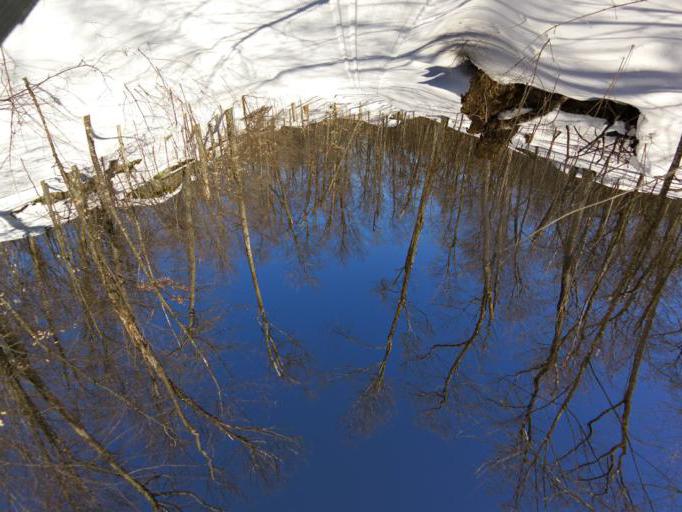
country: CA
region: Quebec
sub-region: Outaouais
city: Wakefield
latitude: 45.5048
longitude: -75.8684
